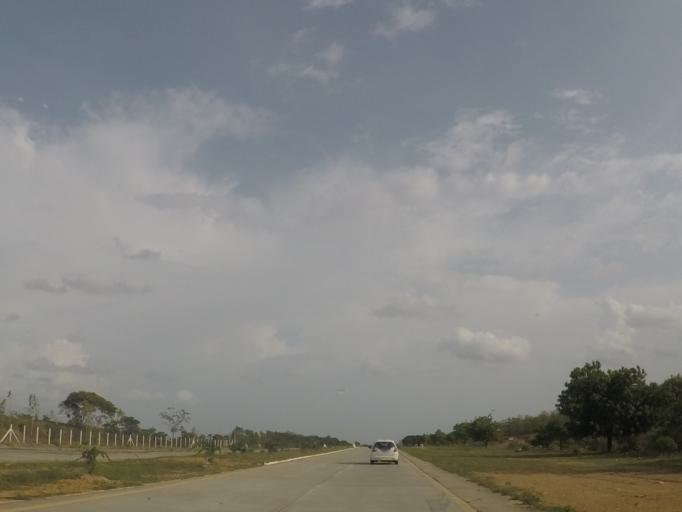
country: MM
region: Mandalay
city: Yamethin
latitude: 20.5135
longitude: 95.8225
